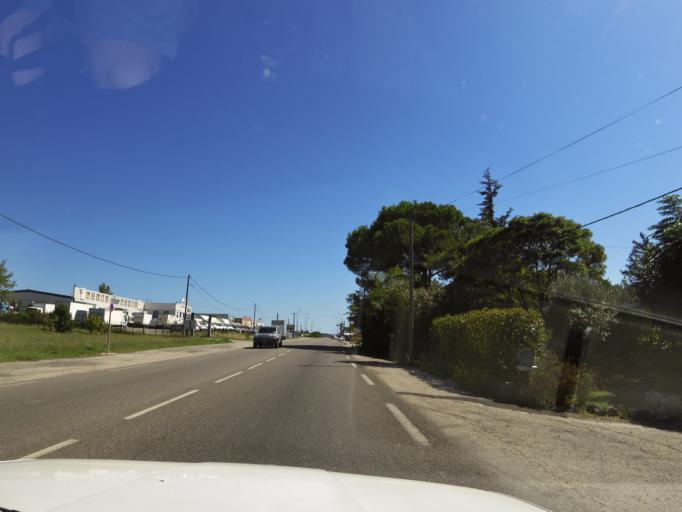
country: FR
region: Languedoc-Roussillon
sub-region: Departement du Gard
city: Saint-Hilaire-de-Brethmas
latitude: 44.0965
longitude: 4.1065
